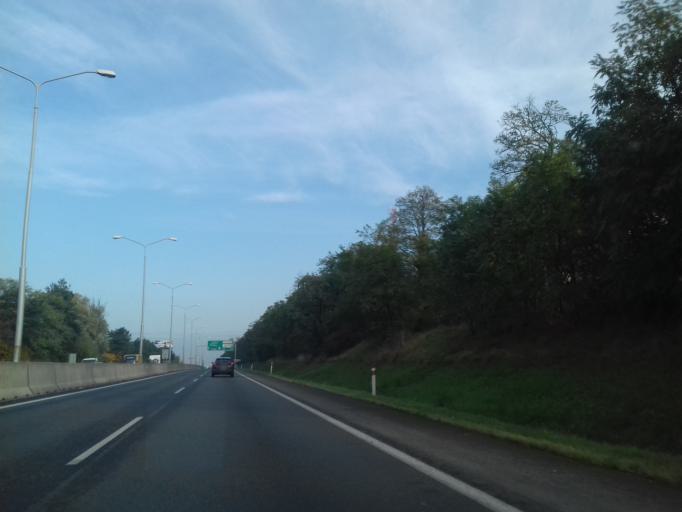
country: AT
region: Lower Austria
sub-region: Politischer Bezirk Bruck an der Leitha
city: Wolfsthal
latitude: 48.1931
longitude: 17.0443
